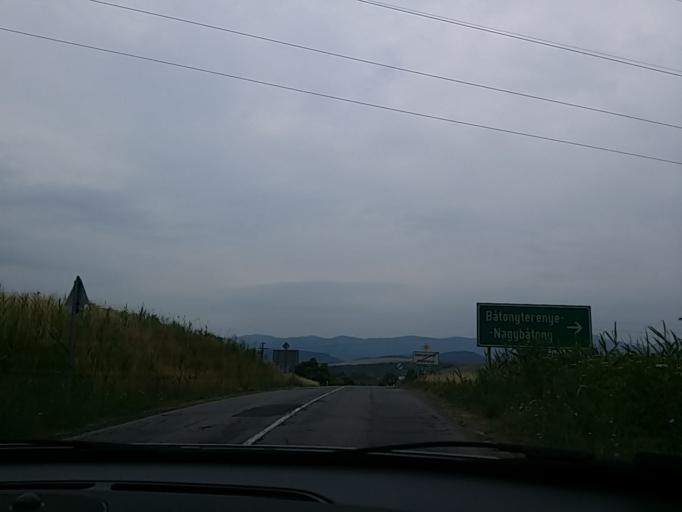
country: HU
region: Nograd
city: Batonyterenye
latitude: 48.0032
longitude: 19.8487
